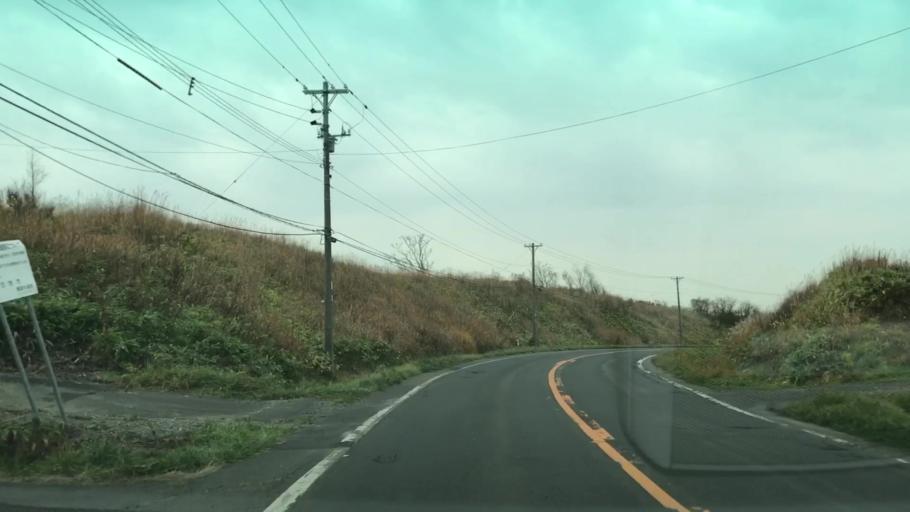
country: JP
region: Hokkaido
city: Ishikari
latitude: 43.3856
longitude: 141.4329
